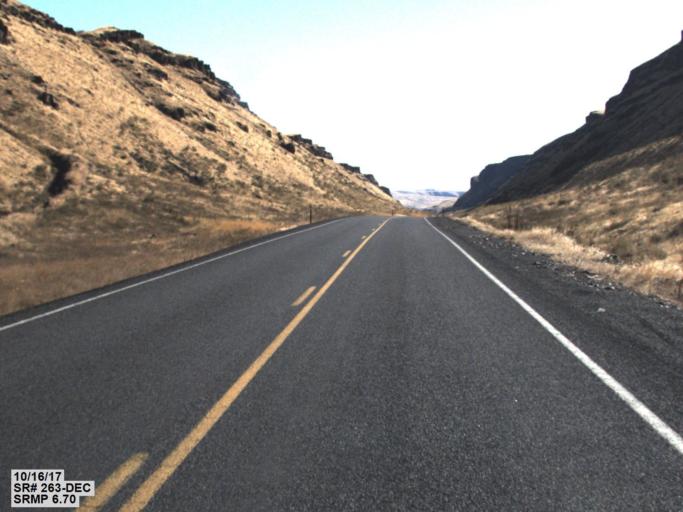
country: US
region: Washington
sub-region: Franklin County
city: Connell
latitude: 46.6109
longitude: -118.5542
